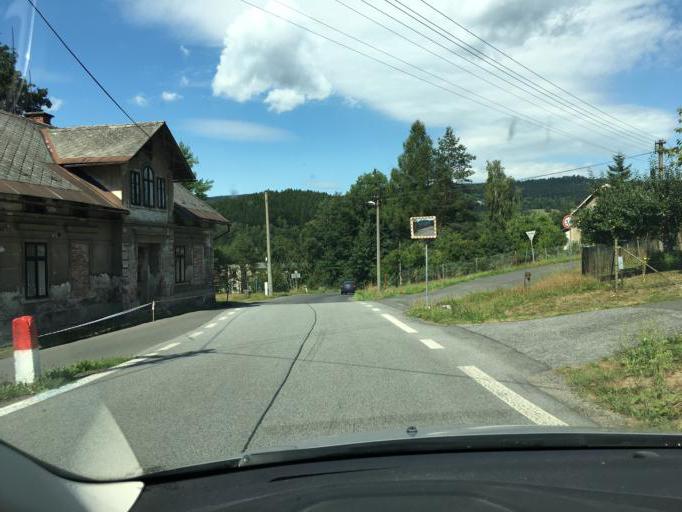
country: CZ
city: Plavy
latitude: 50.7030
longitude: 15.3234
